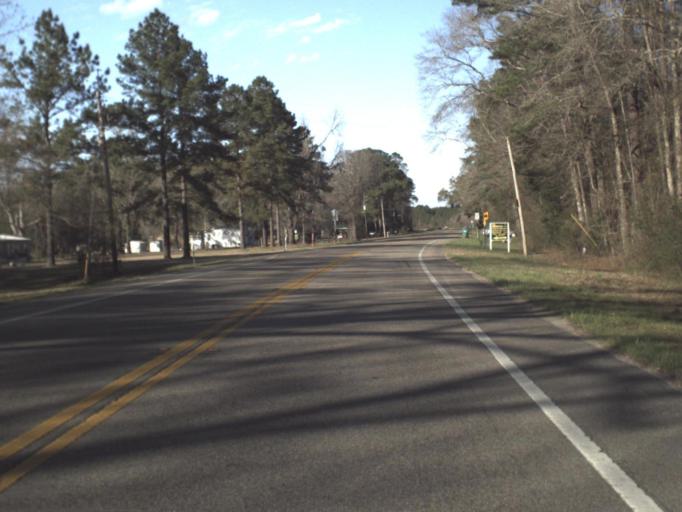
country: US
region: Florida
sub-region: Jackson County
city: Marianna
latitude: 30.6850
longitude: -85.2386
